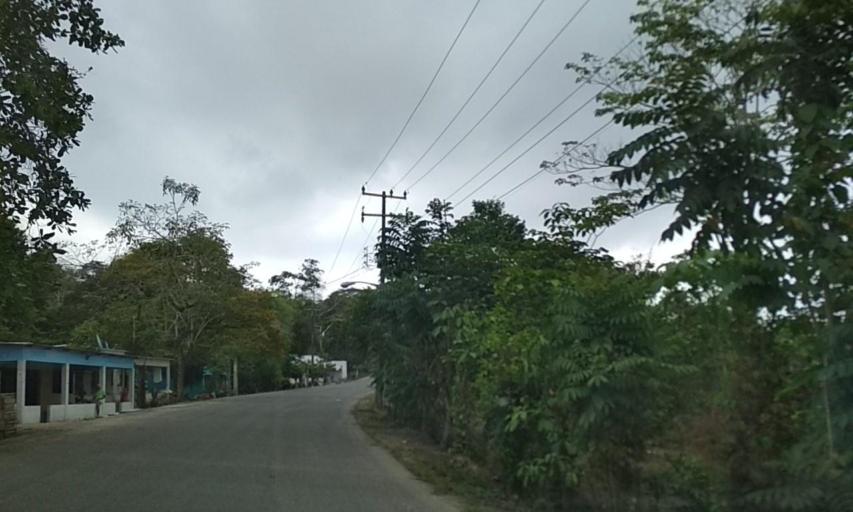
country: MX
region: Tabasco
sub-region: Huimanguillo
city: Francisco Rueda
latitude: 17.5793
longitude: -94.0963
